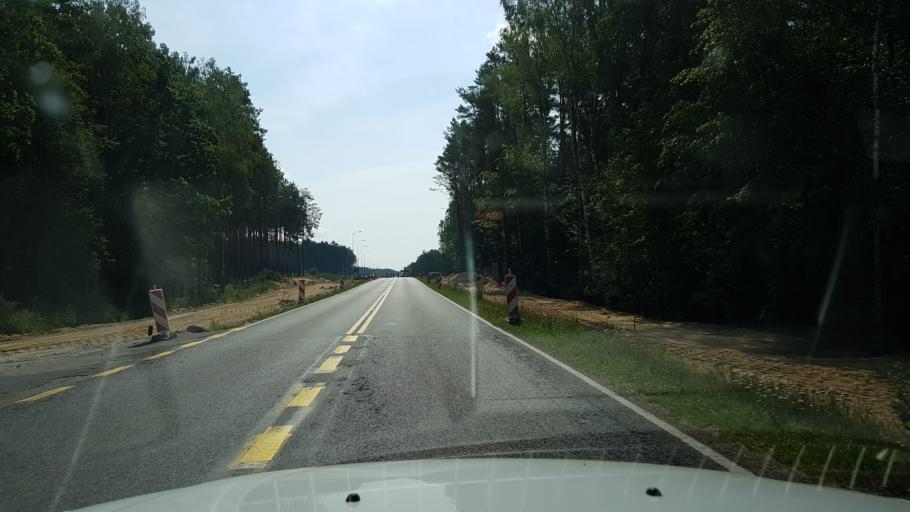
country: PL
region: West Pomeranian Voivodeship
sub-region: Powiat walecki
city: Walcz
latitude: 53.3016
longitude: 16.4111
